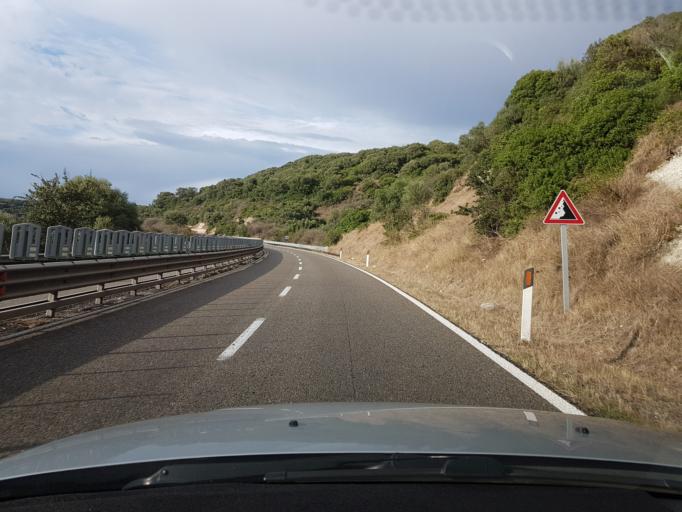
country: IT
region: Sardinia
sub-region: Provincia di Oristano
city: Bauladu
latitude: 40.0448
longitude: 8.7088
